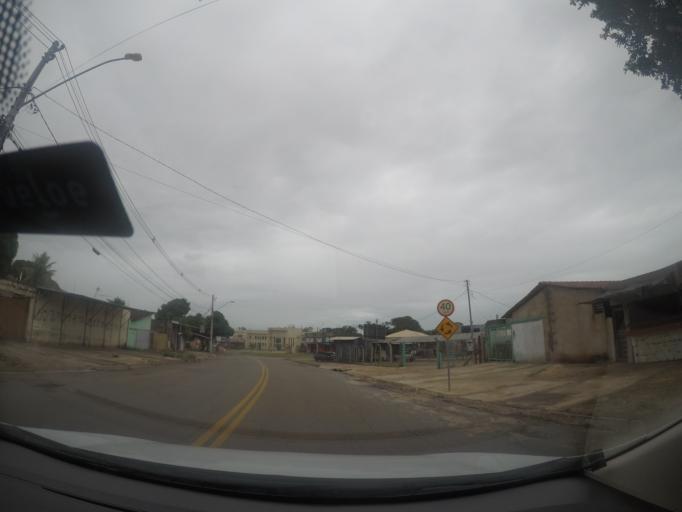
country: BR
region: Goias
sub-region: Goiania
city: Goiania
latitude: -16.6163
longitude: -49.2951
